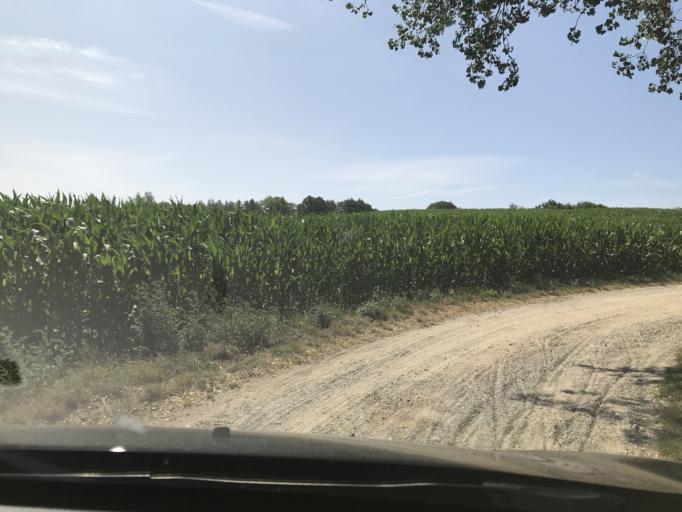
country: DK
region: South Denmark
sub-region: AEro Kommune
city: AEroskobing
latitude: 54.9062
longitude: 10.3220
